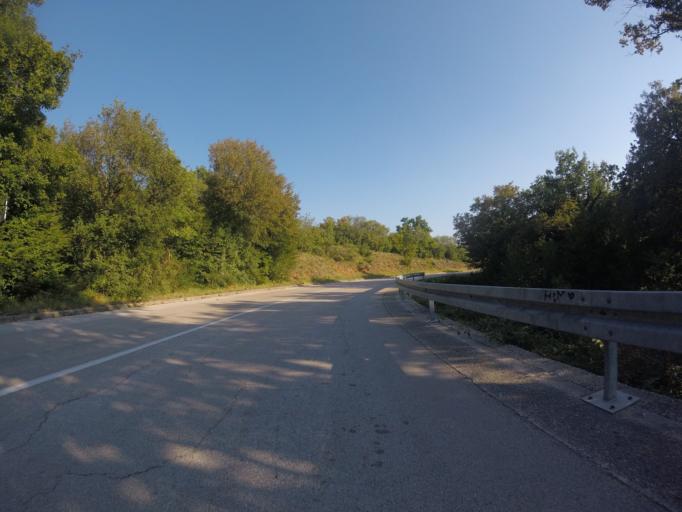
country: HR
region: Primorsko-Goranska
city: Selce
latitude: 45.1867
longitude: 14.7300
